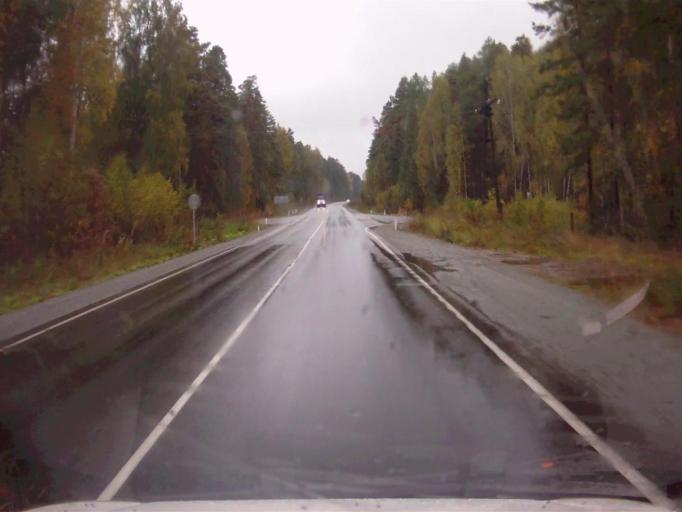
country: RU
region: Chelyabinsk
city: Kyshtym
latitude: 55.6357
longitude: 60.5972
